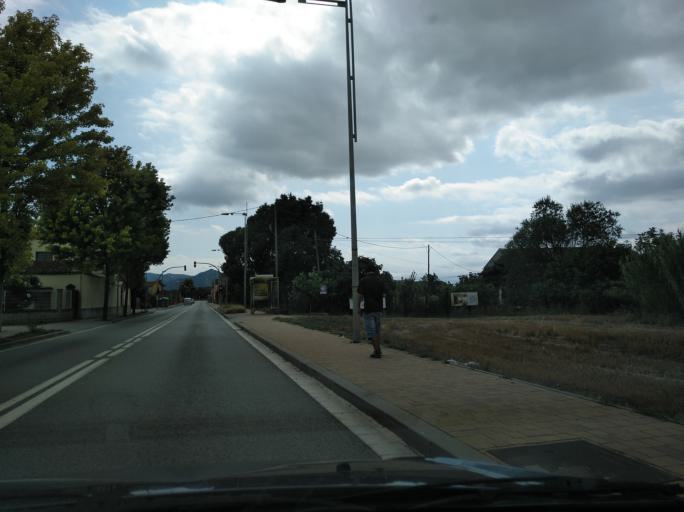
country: ES
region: Catalonia
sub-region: Provincia de Barcelona
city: Granollers
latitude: 41.5799
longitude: 2.2832
